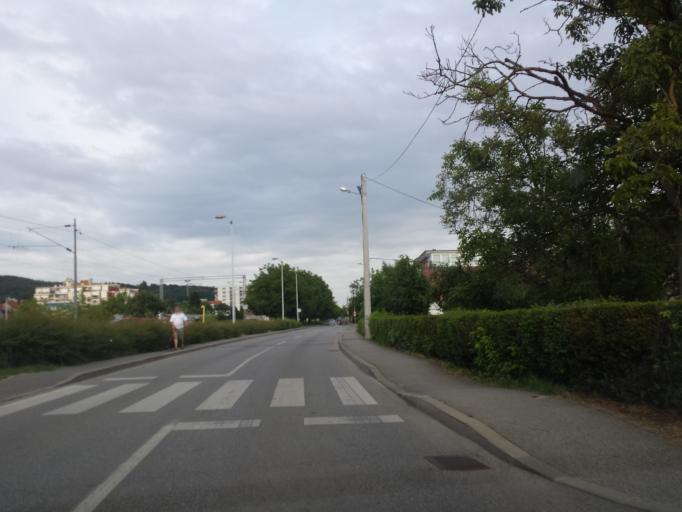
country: HR
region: Grad Zagreb
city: Stenjevec
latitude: 45.8119
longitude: 15.8979
